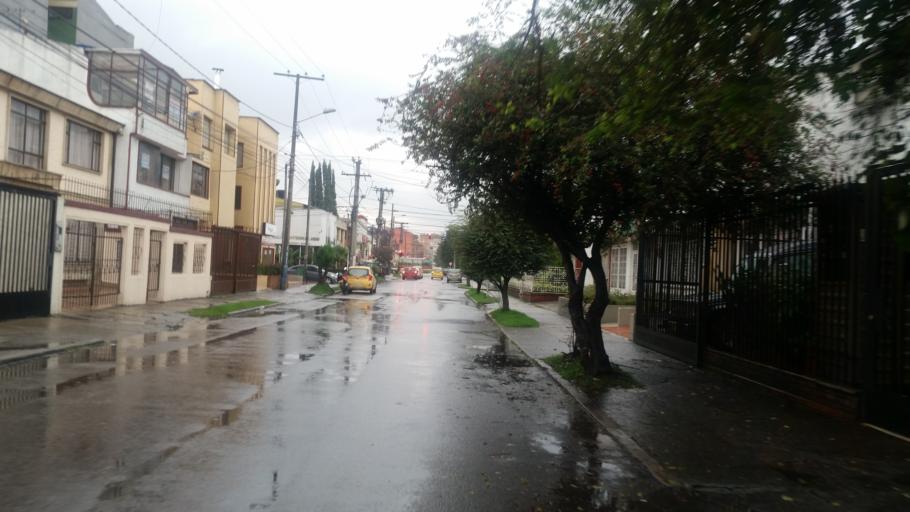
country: CO
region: Bogota D.C.
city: Bogota
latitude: 4.6313
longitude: -74.0950
